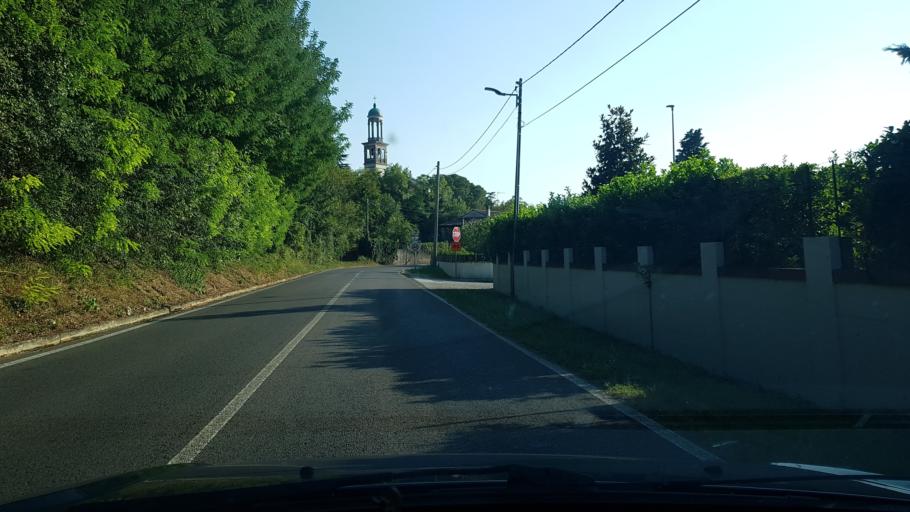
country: IT
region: Friuli Venezia Giulia
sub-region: Provincia di Gorizia
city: Gradisca d'Isonzo
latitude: 45.8886
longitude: 13.5179
